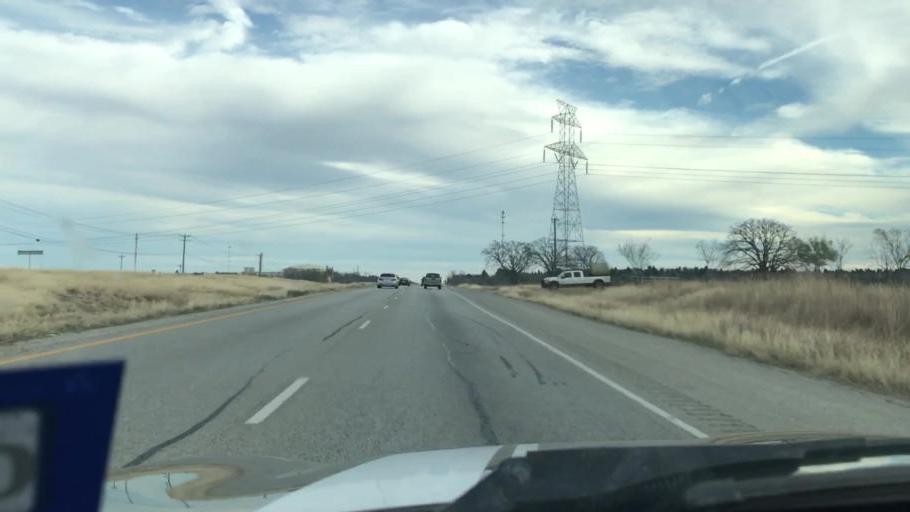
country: US
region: Texas
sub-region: Bastrop County
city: Elgin
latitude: 30.3309
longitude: -97.3479
